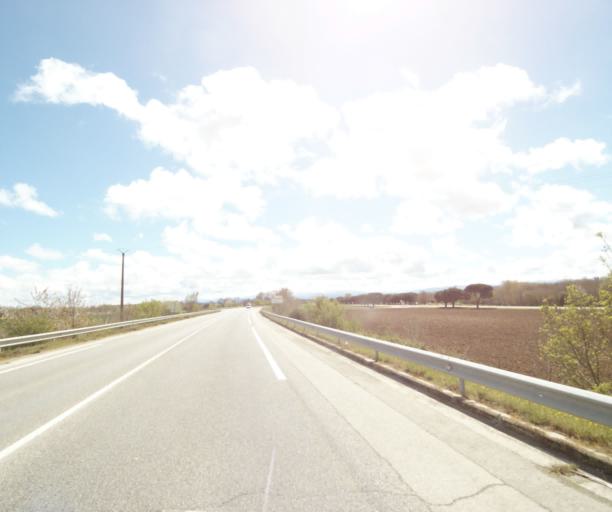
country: FR
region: Midi-Pyrenees
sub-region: Departement de l'Ariege
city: Saverdun
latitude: 43.2298
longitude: 1.6041
